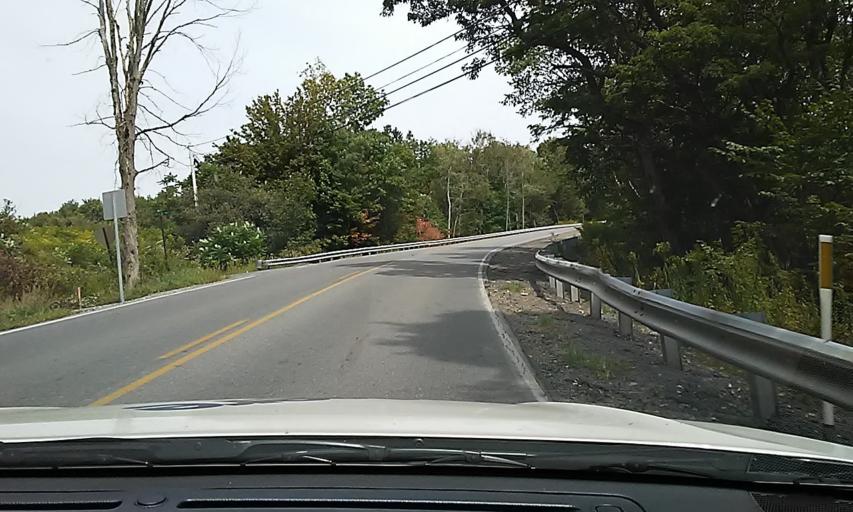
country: US
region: Pennsylvania
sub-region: Elk County
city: Saint Marys
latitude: 41.3362
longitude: -78.6286
